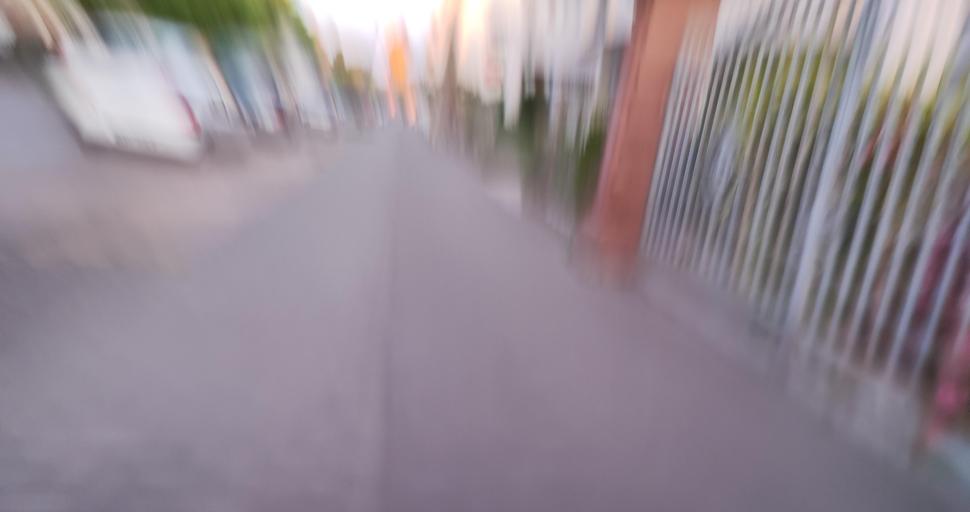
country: FR
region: Alsace
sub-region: Departement du Bas-Rhin
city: Selestat
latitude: 48.2603
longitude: 7.4502
